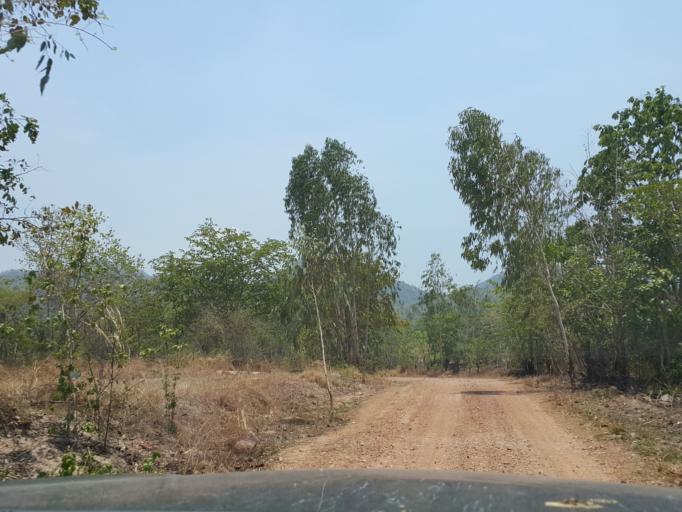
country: TH
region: Lampang
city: Thoen
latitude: 17.6381
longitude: 99.2754
